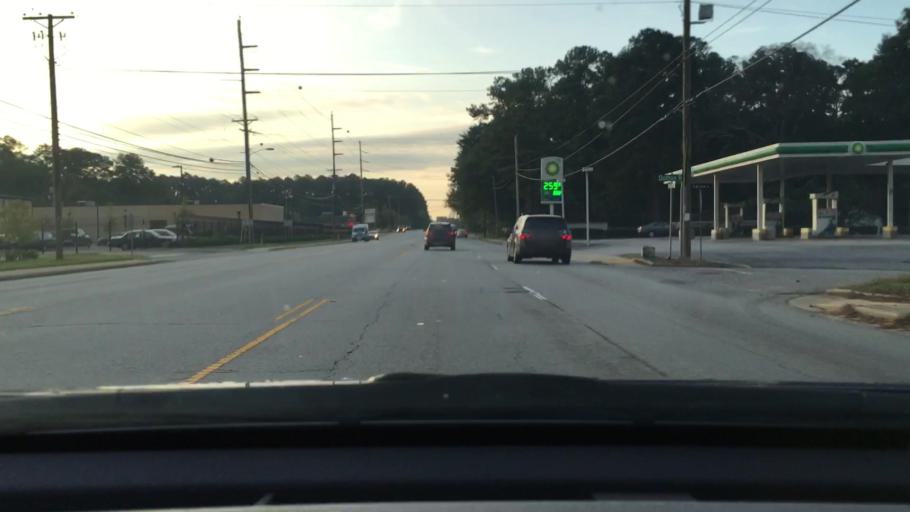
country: US
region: South Carolina
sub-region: Lexington County
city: Saint Andrews
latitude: 34.0659
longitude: -81.1167
